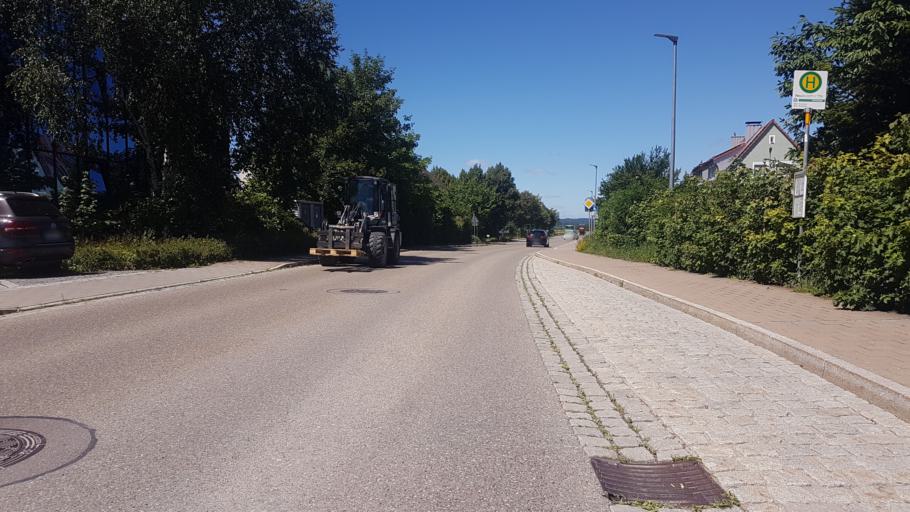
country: DE
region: Bavaria
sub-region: Regierungsbezirk Mittelfranken
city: Herrieden
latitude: 49.2350
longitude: 10.4915
